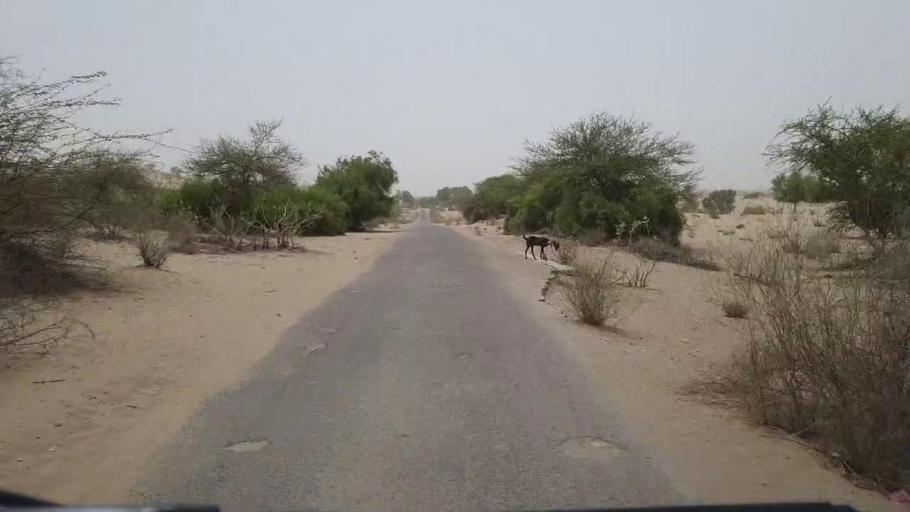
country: PK
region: Sindh
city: Naukot
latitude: 24.7816
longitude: 69.5338
